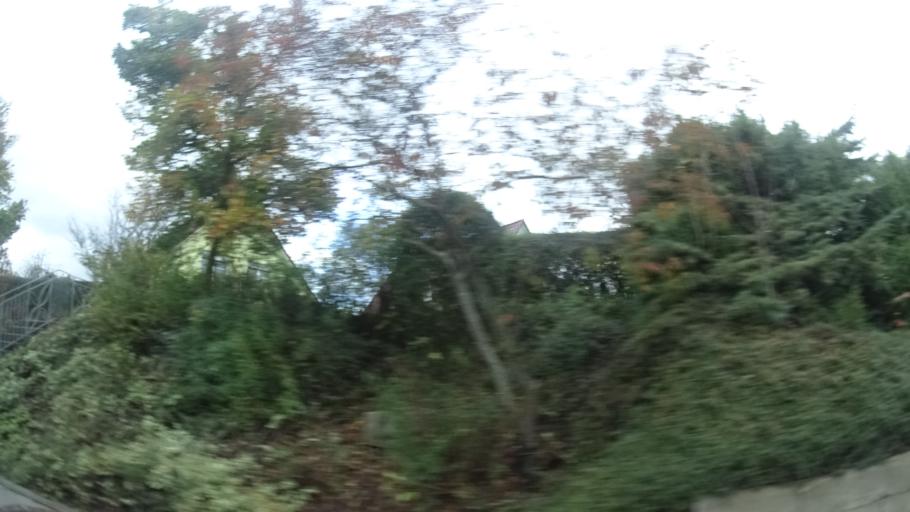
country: DE
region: Bavaria
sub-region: Regierungsbezirk Unterfranken
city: Bad Neustadt an der Saale
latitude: 50.3294
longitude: 10.2071
